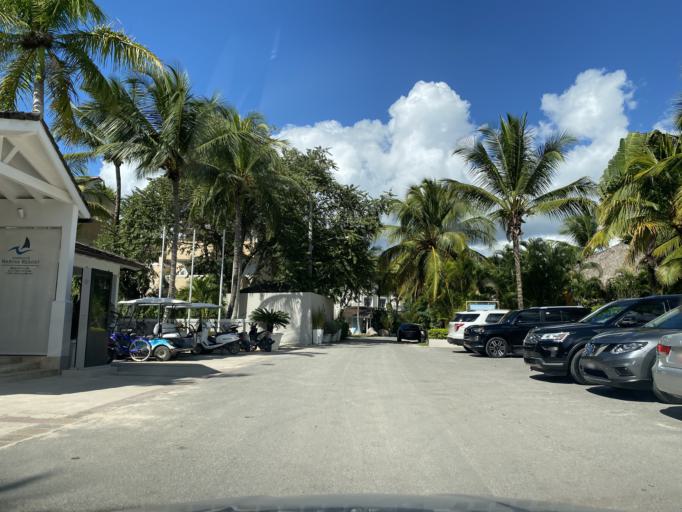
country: DO
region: La Romana
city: La Romana
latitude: 18.3509
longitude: -68.8328
